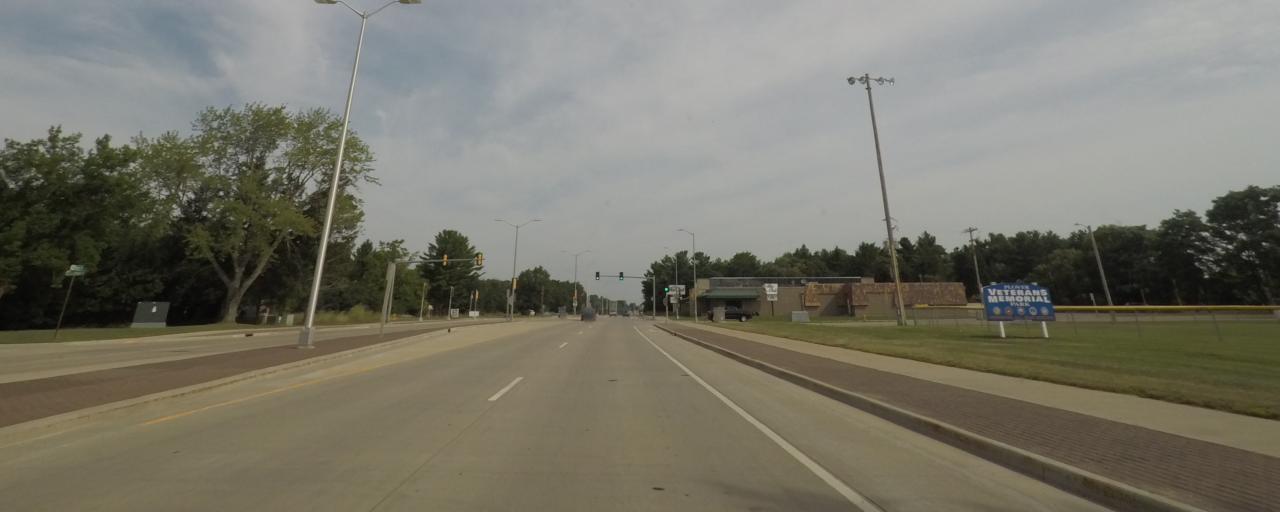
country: US
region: Wisconsin
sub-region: Portage County
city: Plover
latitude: 44.4637
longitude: -89.5443
